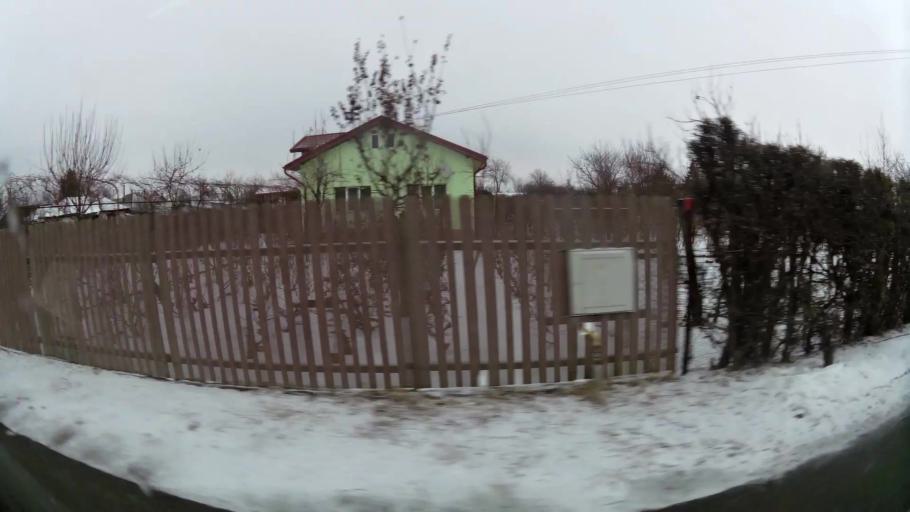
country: RO
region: Prahova
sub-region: Comuna Berceni
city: Corlatesti
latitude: 44.9233
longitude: 26.0710
